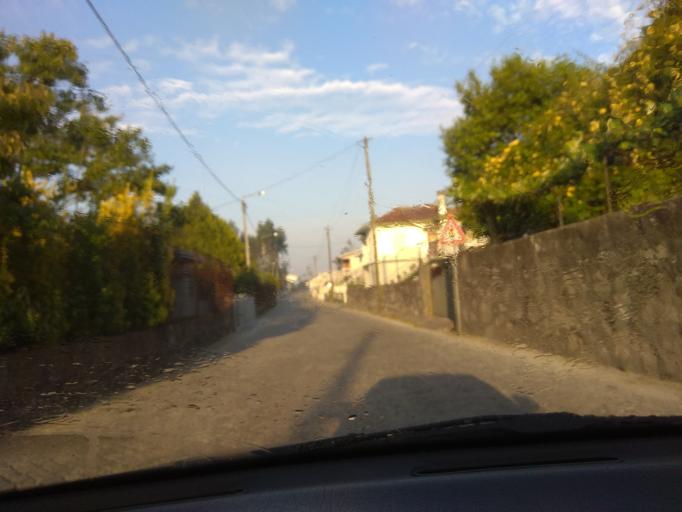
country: PT
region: Porto
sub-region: Maia
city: Nogueira
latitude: 41.2572
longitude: -8.5937
